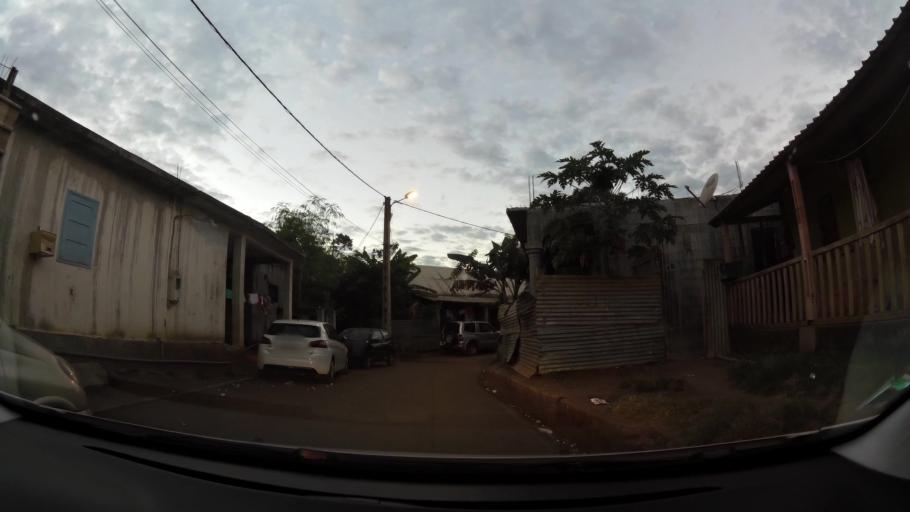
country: YT
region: Bandraboua
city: Bandraboua
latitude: -12.7337
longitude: 45.1391
